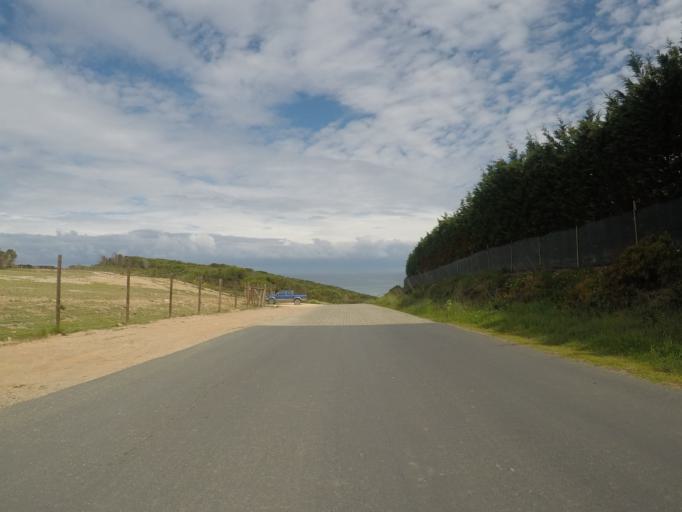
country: PT
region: Beja
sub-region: Odemira
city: Sao Teotonio
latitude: 37.4975
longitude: -8.7905
